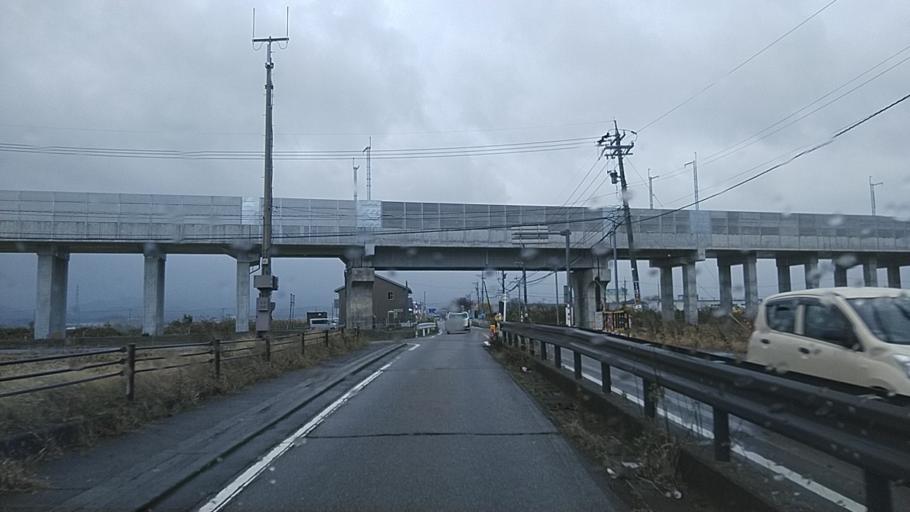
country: JP
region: Ishikawa
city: Komatsu
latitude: 36.3230
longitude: 136.3579
